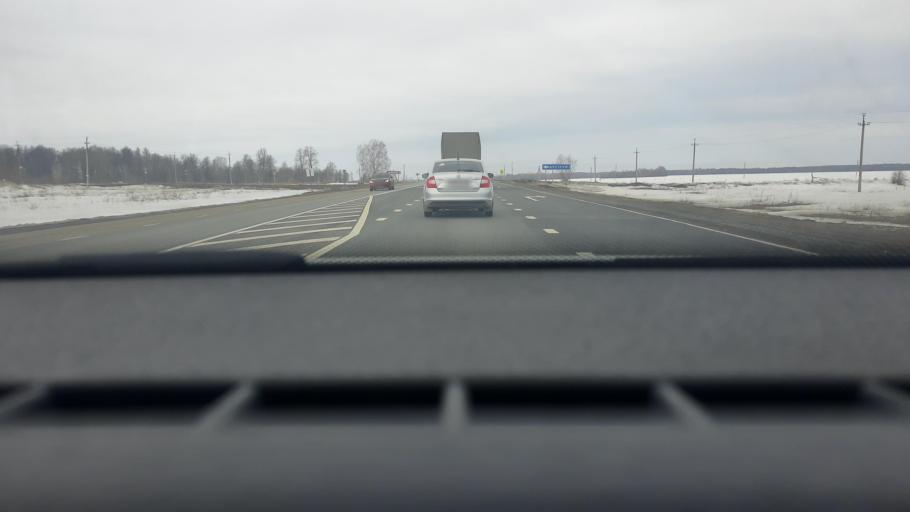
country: RU
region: Bashkortostan
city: Kudeyevskiy
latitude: 54.8173
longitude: 56.7546
